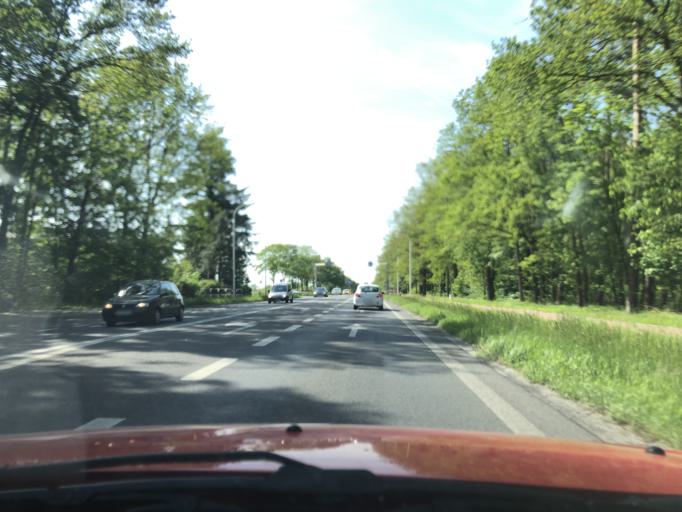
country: PL
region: Greater Poland Voivodeship
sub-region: Powiat pleszewski
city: Goluchow
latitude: 51.8545
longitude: 17.9230
